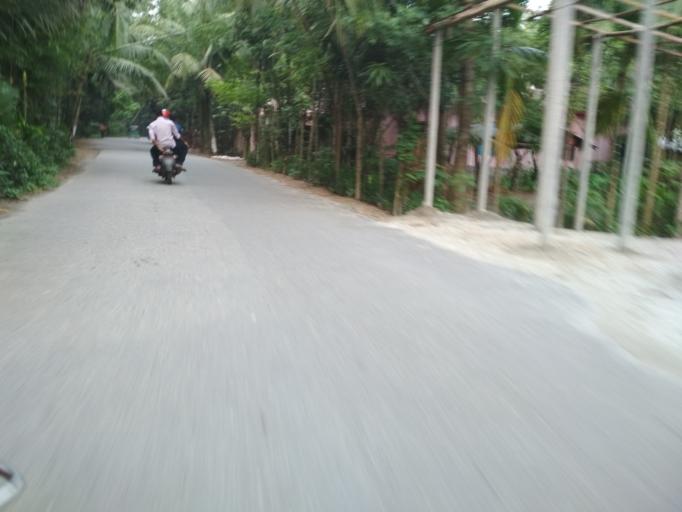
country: BD
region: Chittagong
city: Raipur
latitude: 23.0062
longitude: 90.7087
